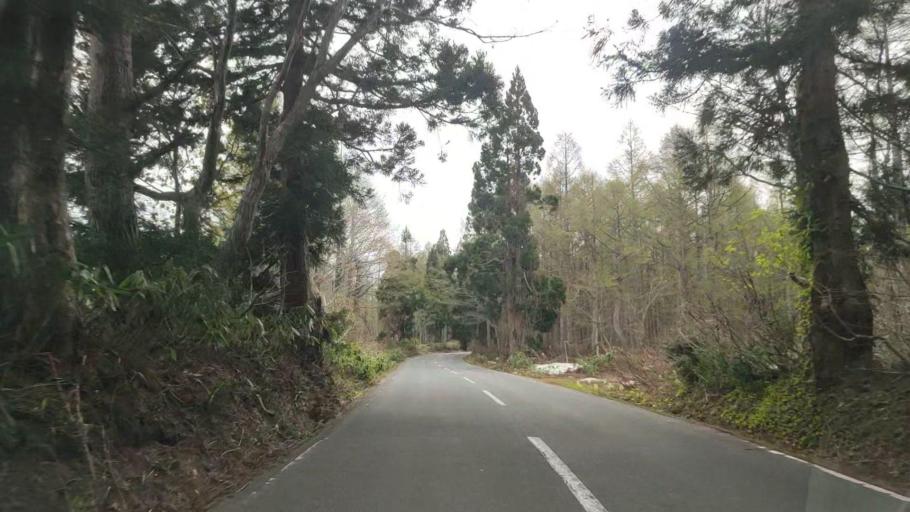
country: JP
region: Aomori
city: Aomori Shi
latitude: 40.7222
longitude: 140.8565
